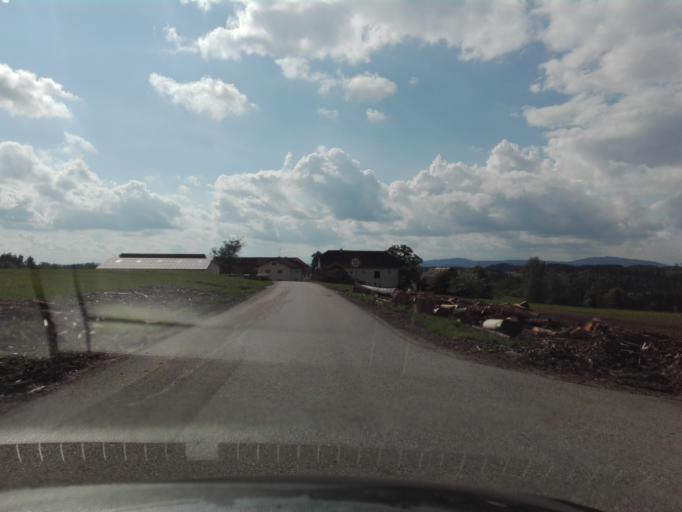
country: AT
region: Upper Austria
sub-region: Politischer Bezirk Rohrbach
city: Pfarrkirchen im Muehlkreis
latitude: 48.4292
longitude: 13.8319
